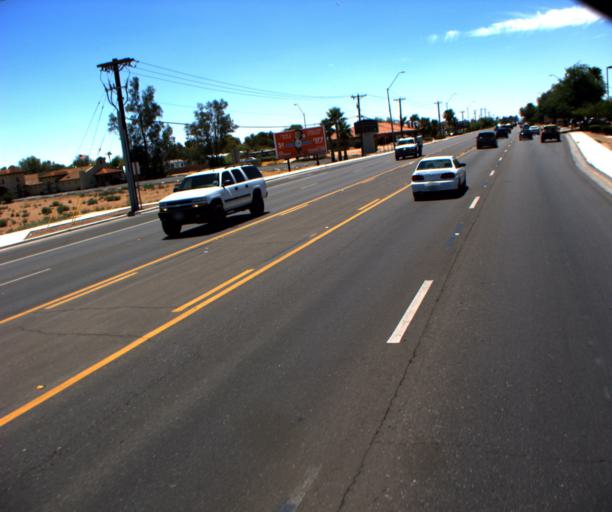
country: US
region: Arizona
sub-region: Pinal County
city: Casa Grande
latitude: 32.8796
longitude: -111.7183
